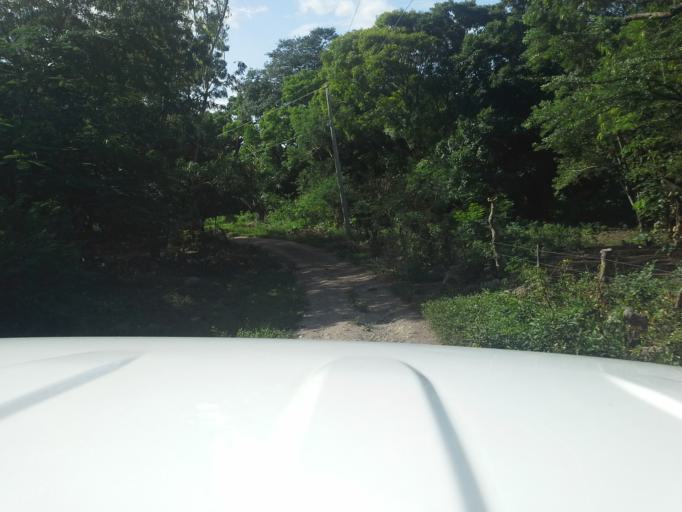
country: NI
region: Matagalpa
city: Terrabona
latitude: 12.6668
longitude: -86.0426
